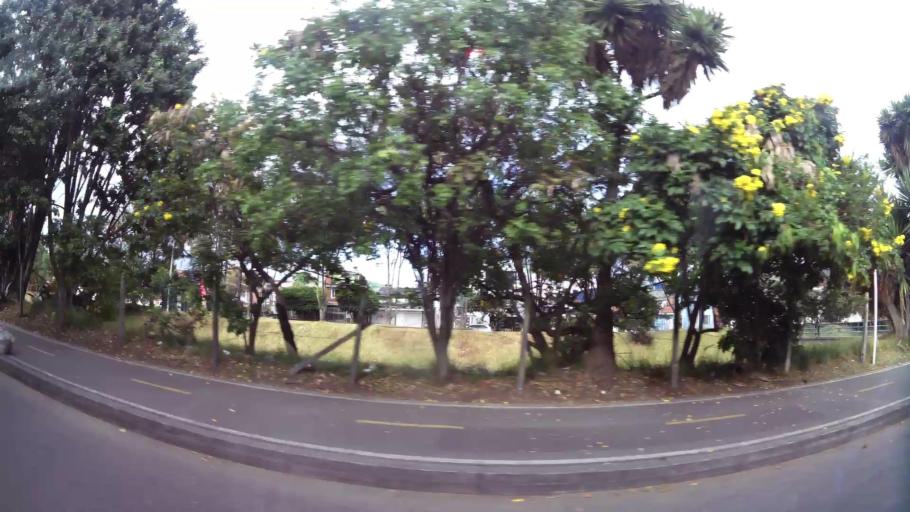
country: CO
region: Bogota D.C.
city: Bogota
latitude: 4.6043
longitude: -74.1184
